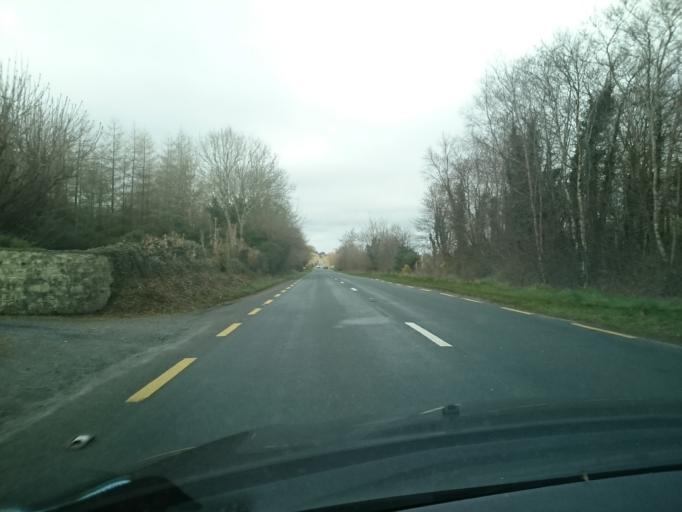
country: IE
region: Connaught
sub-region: Maigh Eo
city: Claremorris
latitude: 53.7653
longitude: -9.0495
